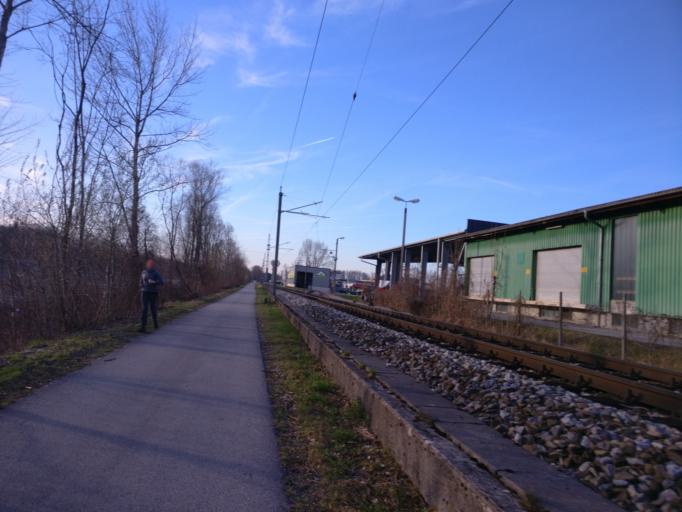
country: AT
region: Salzburg
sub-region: Politischer Bezirk Salzburg-Umgebung
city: Bergheim
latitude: 47.8426
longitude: 13.0164
